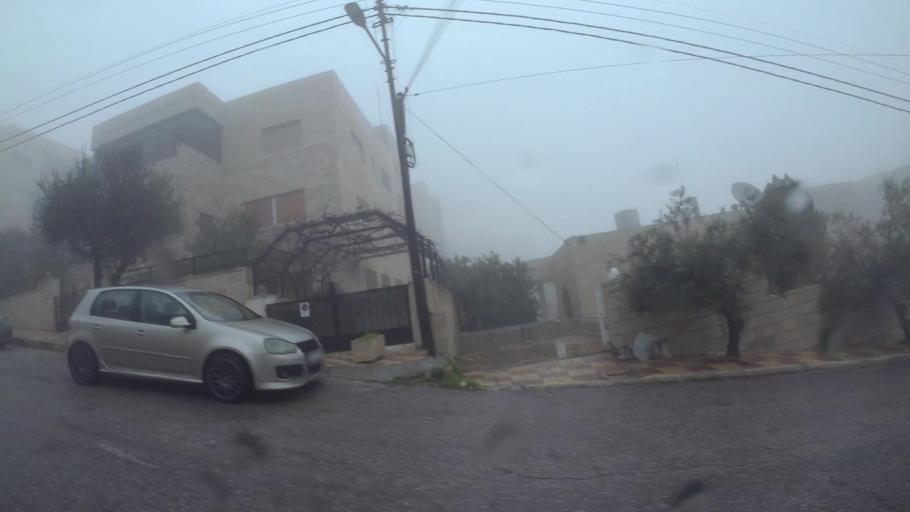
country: JO
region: Amman
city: Al Jubayhah
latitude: 32.0048
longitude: 35.8893
